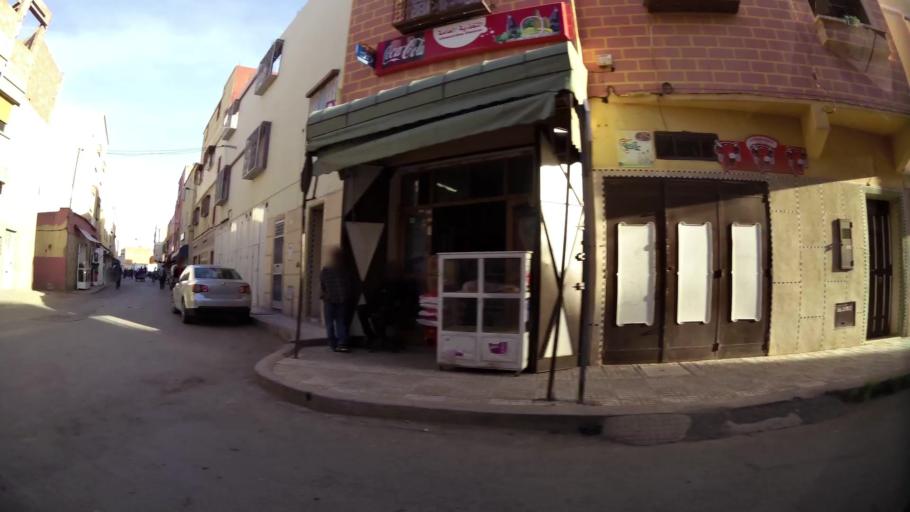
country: MA
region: Oriental
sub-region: Oujda-Angad
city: Oujda
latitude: 34.6776
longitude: -1.9045
